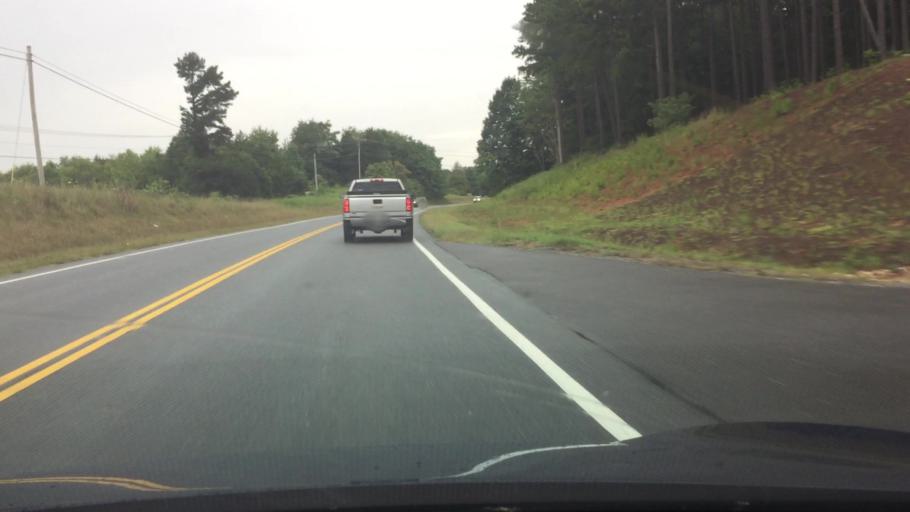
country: US
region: Virginia
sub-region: City of Bedford
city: Bedford
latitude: 37.3640
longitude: -79.4400
